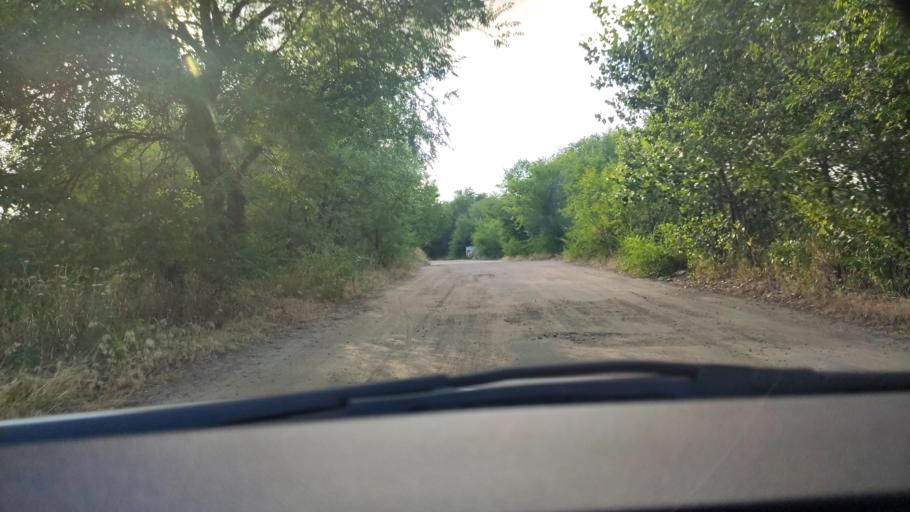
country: RU
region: Voronezj
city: Pridonskoy
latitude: 51.6841
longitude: 39.0628
